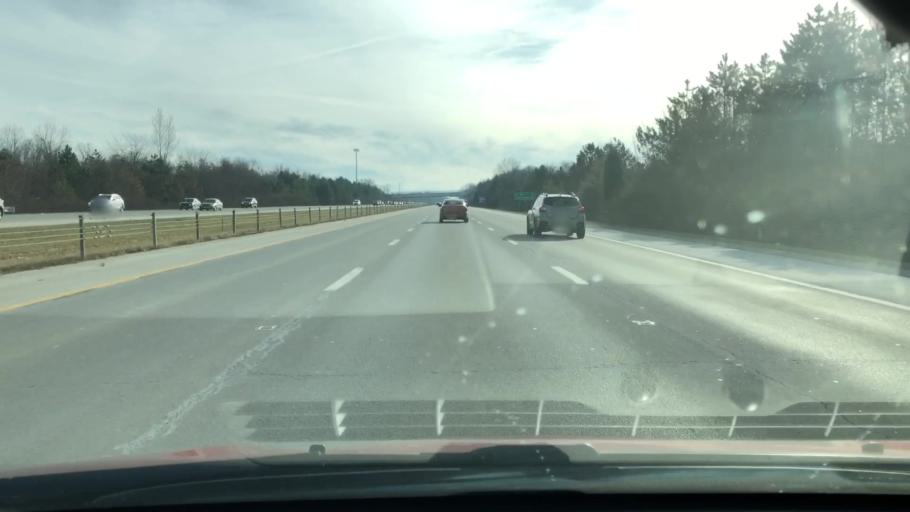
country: US
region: Ohio
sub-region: Greene County
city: Beavercreek
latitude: 39.7212
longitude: -84.0914
